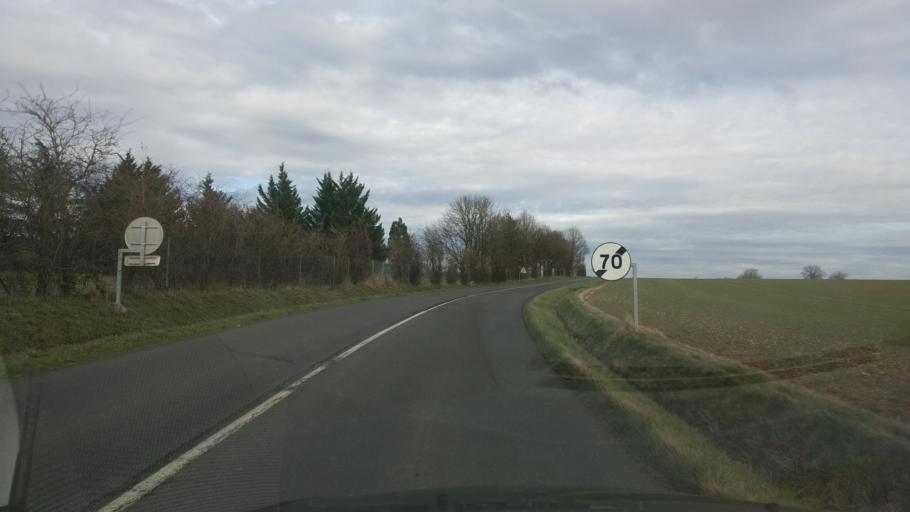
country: FR
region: Poitou-Charentes
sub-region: Departement de la Vienne
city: Saint-Georges-les-Baillargeaux
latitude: 46.6618
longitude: 0.3938
